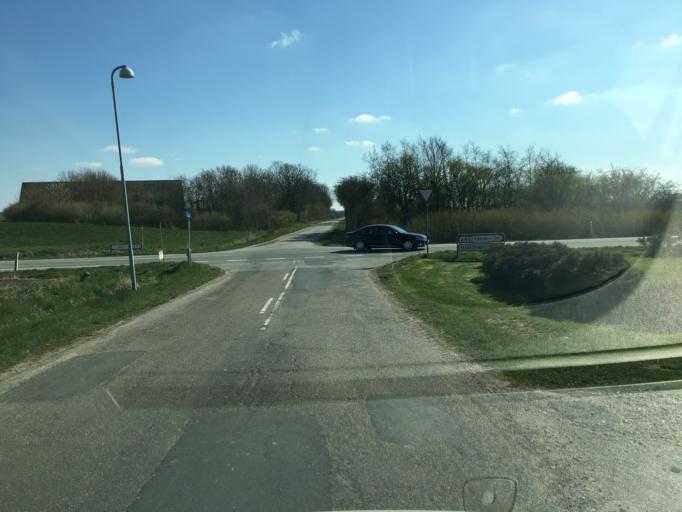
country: DK
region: South Denmark
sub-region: Aabenraa Kommune
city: Rodekro
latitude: 55.0262
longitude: 9.3481
